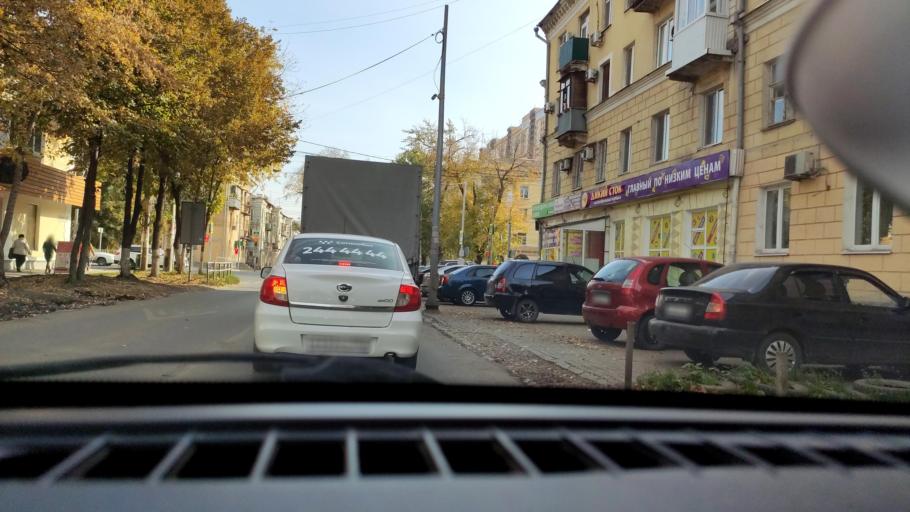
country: RU
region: Samara
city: Samara
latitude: 53.2188
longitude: 50.2598
